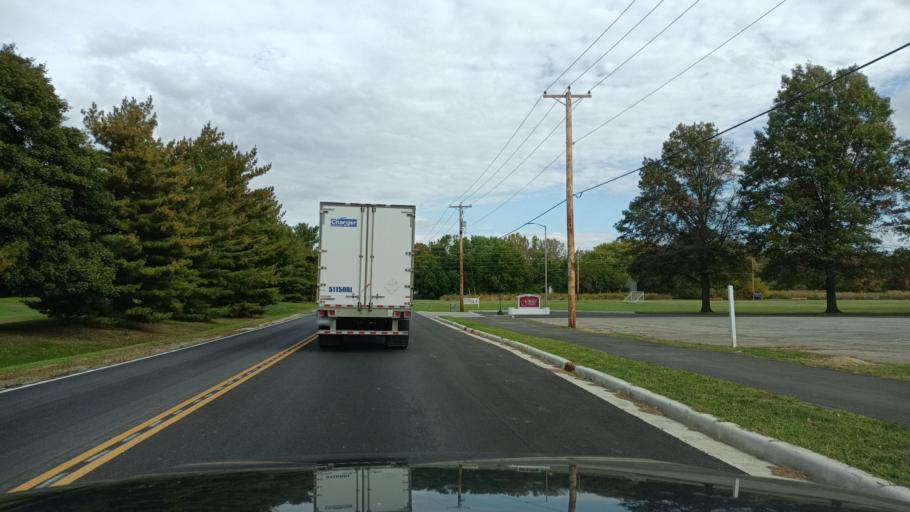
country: US
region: Indiana
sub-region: Delaware County
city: Yorktown
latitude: 40.1877
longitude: -85.4617
